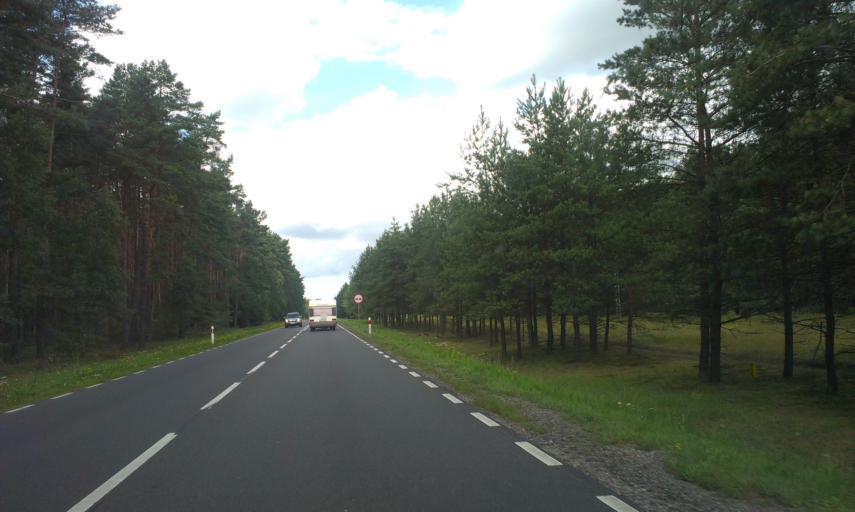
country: PL
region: West Pomeranian Voivodeship
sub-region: Powiat koszalinski
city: Sianow
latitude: 54.1016
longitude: 16.3478
